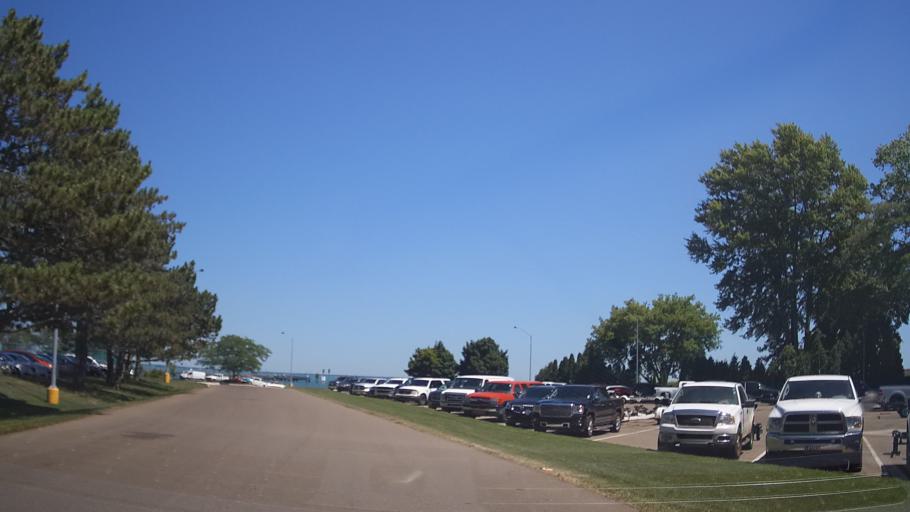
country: US
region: Michigan
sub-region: Macomb County
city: New Baltimore
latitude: 42.6655
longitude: -82.7607
